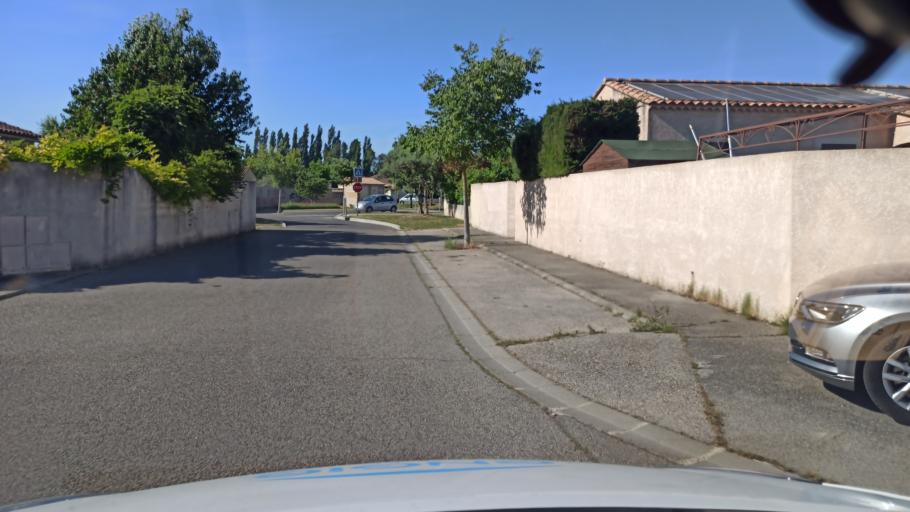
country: FR
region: Provence-Alpes-Cote d'Azur
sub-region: Departement du Vaucluse
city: Morieres-les-Avignon
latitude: 43.9558
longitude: 4.8929
